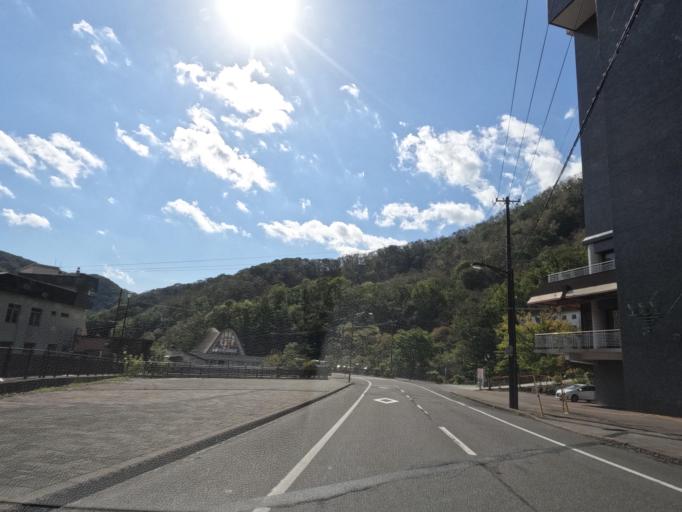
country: JP
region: Hokkaido
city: Shiraoi
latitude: 42.4922
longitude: 141.1427
